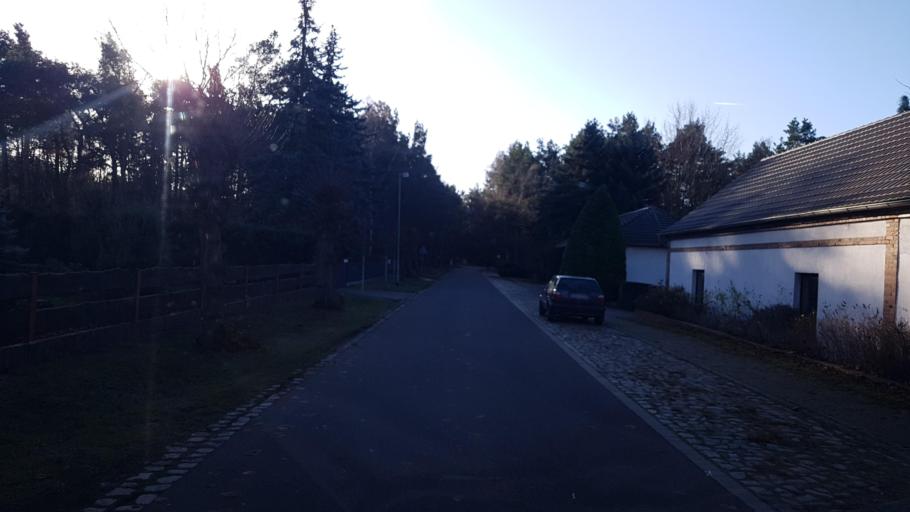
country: DE
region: Brandenburg
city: Heinersbruck
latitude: 51.7431
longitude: 14.5160
